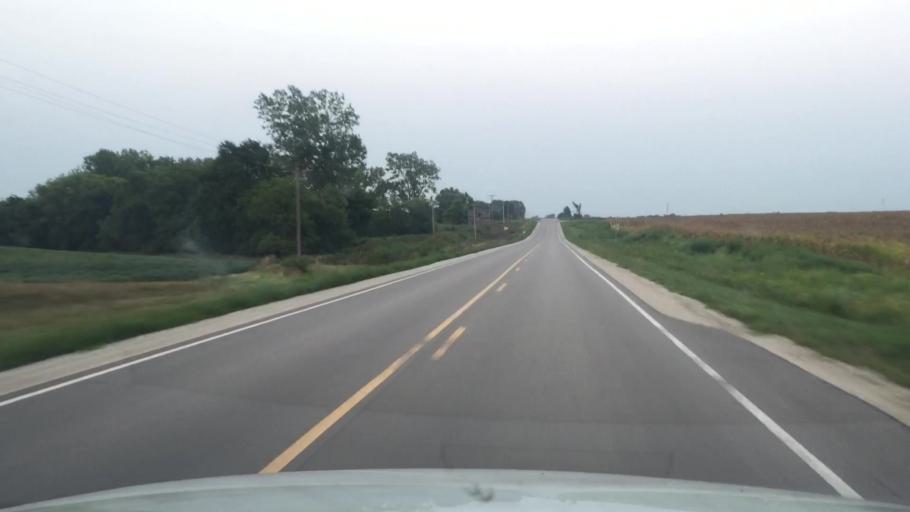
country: US
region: Iowa
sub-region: Warren County
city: Indianola
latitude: 41.1826
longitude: -93.4855
